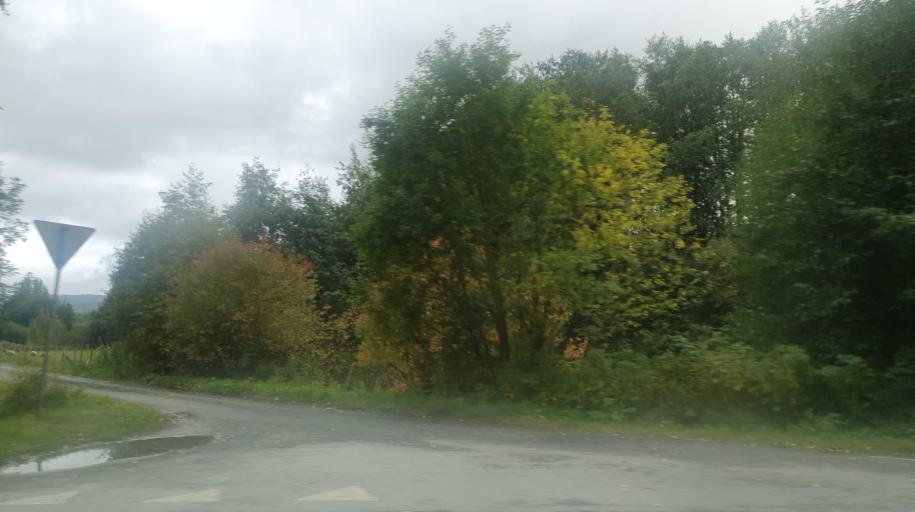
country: NO
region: Nord-Trondelag
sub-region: Verdal
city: Verdal
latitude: 63.7955
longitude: 11.5055
